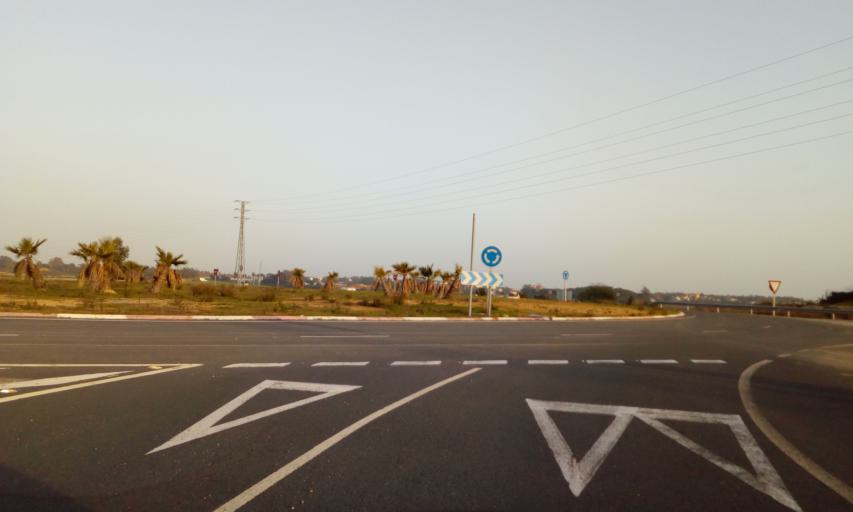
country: ES
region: Andalusia
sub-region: Provincia de Huelva
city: Lepe
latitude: 37.2310
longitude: -7.2293
